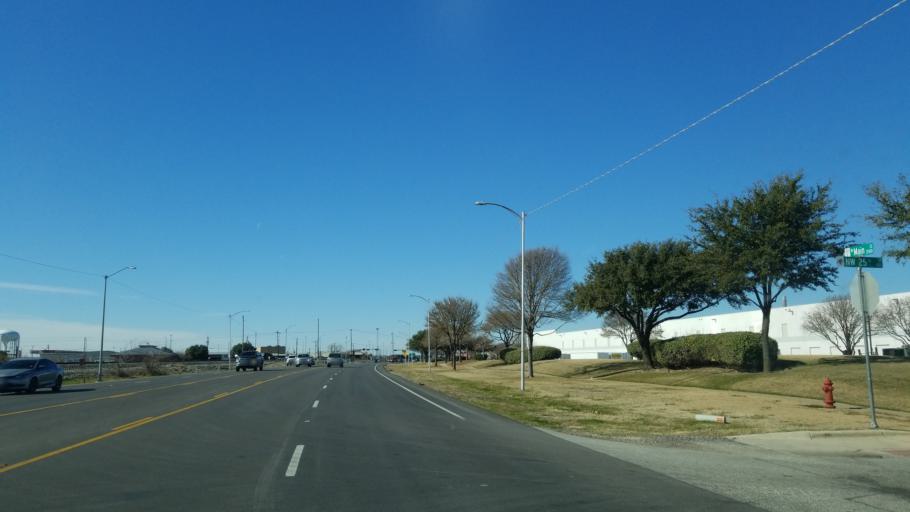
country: US
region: Texas
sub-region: Dallas County
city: Grand Prairie
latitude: 32.7392
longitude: -97.0424
